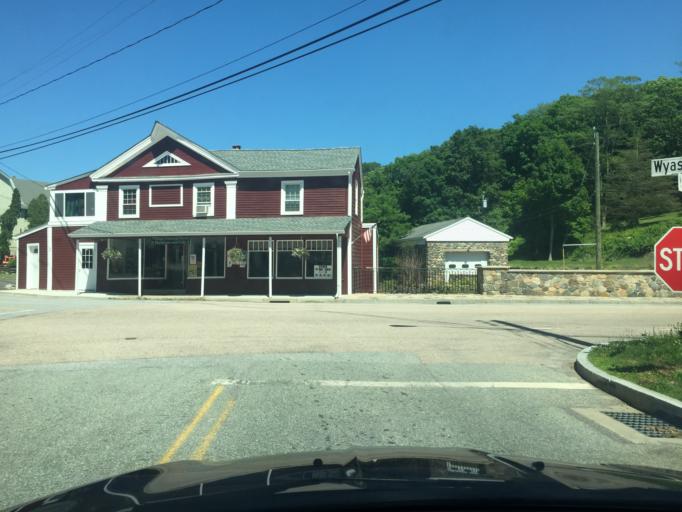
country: US
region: Connecticut
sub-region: New London County
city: Pawcatuck
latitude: 41.4411
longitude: -71.8815
